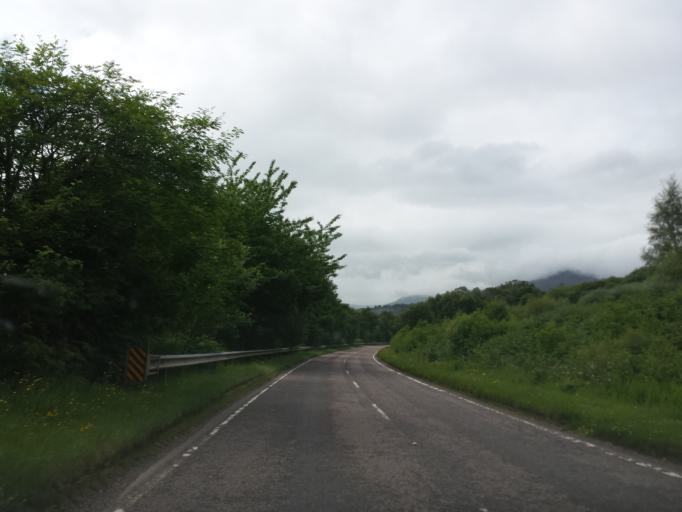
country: GB
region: Scotland
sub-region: Highland
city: Fort William
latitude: 56.8576
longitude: -5.3118
